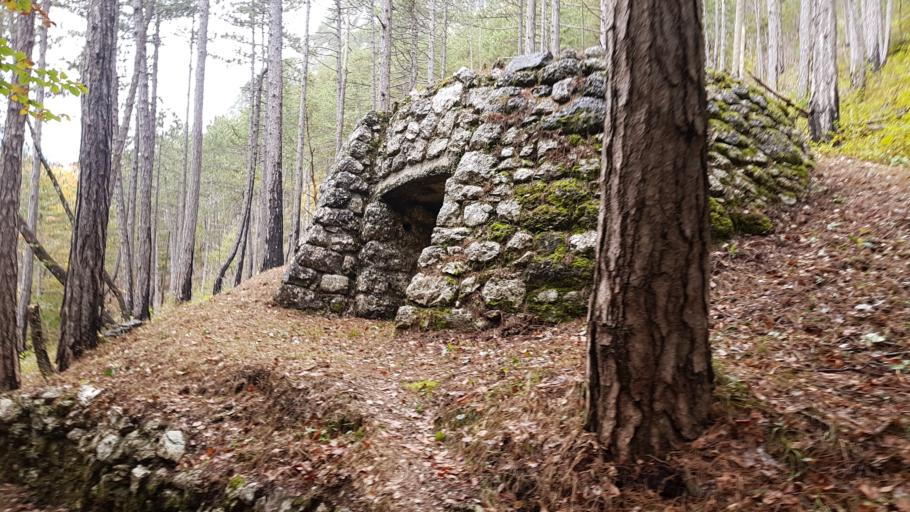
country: IT
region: Friuli Venezia Giulia
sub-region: Provincia di Udine
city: Chiusaforte
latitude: 46.4109
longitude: 13.3402
